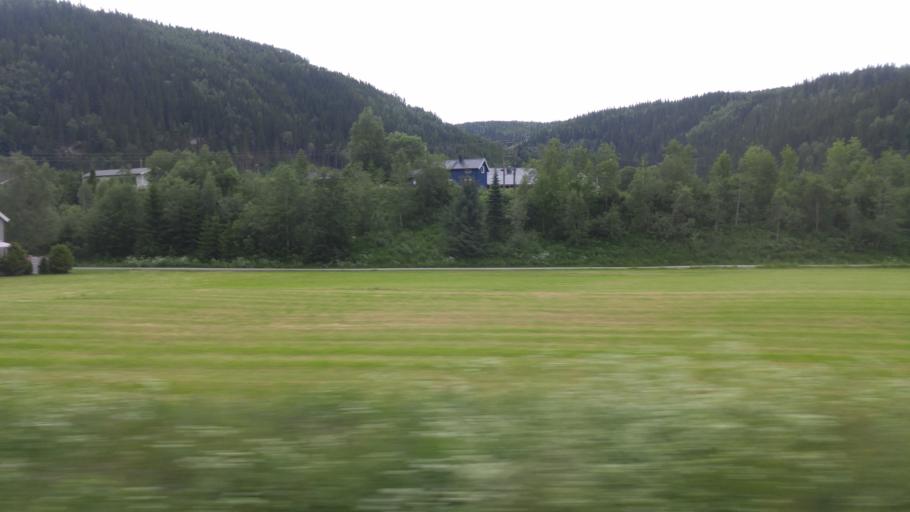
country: NO
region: Nord-Trondelag
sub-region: Levanger
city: Skogn
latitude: 63.4579
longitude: 11.3479
